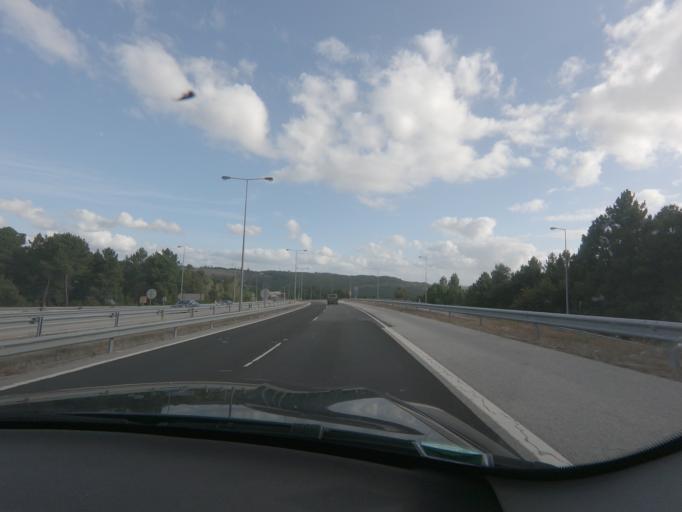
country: PT
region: Viseu
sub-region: Castro Daire
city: Castro Daire
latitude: 40.8572
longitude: -7.9294
